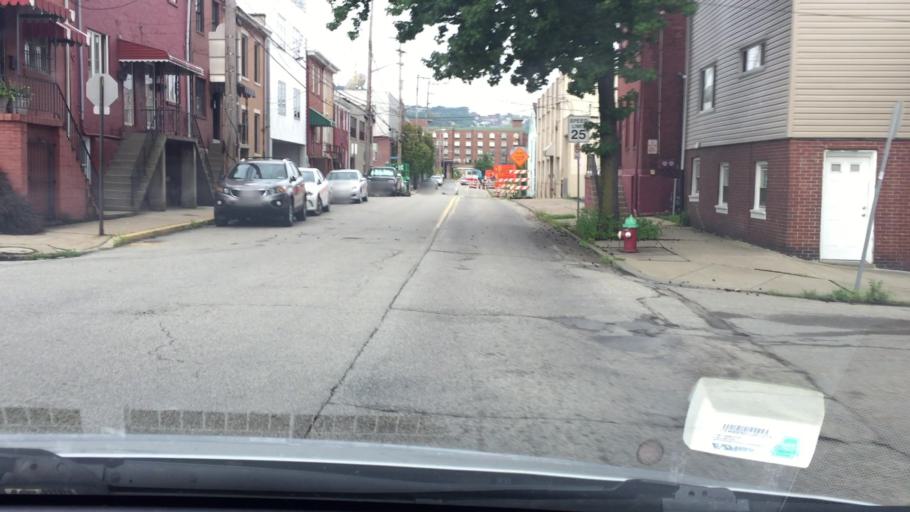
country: US
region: Pennsylvania
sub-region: Allegheny County
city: Pittsburgh
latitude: 40.4301
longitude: -79.9852
